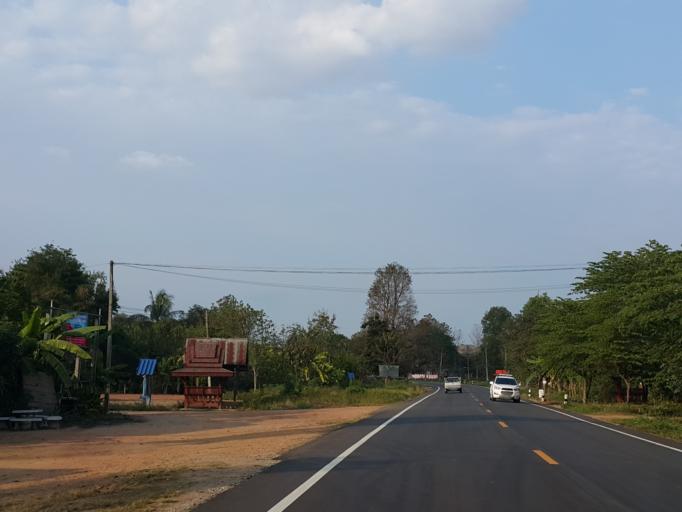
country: TH
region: Lampang
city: Lampang
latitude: 18.4824
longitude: 99.4713
